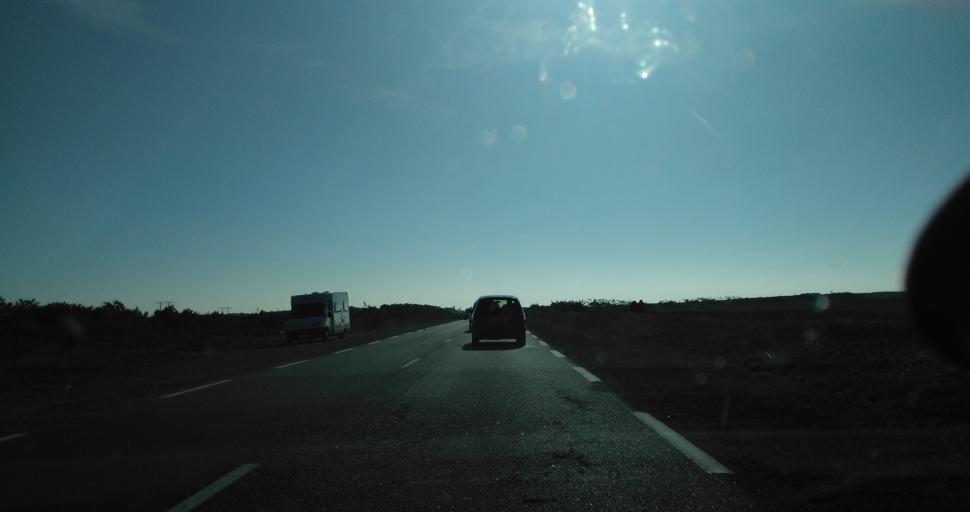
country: FR
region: Brittany
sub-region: Departement du Morbihan
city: Plouharnel
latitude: 47.5850
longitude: -3.1341
